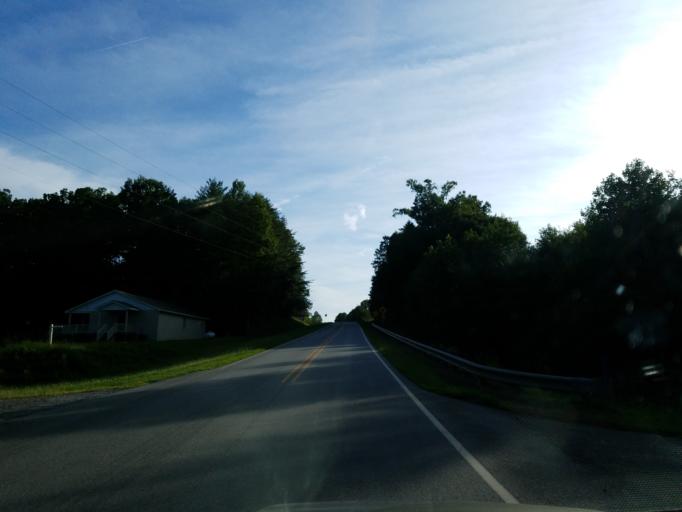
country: US
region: Georgia
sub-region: White County
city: Cleveland
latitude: 34.6012
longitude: -83.8620
